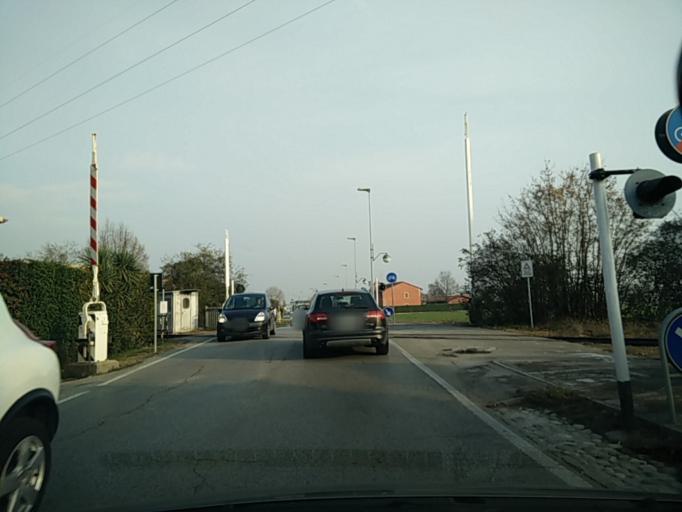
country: IT
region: Veneto
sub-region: Provincia di Treviso
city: Castelfranco Veneto
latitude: 45.6735
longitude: 11.9535
